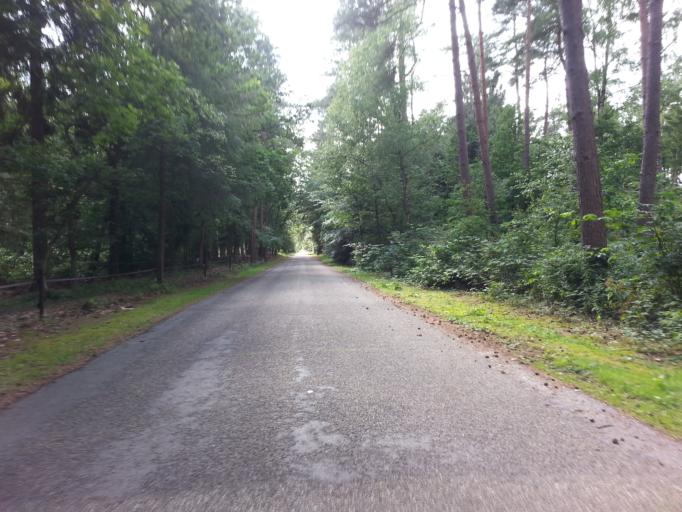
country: NL
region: Utrecht
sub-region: Gemeente Utrechtse Heuvelrug
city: Maarn
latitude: 52.0768
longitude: 5.3683
